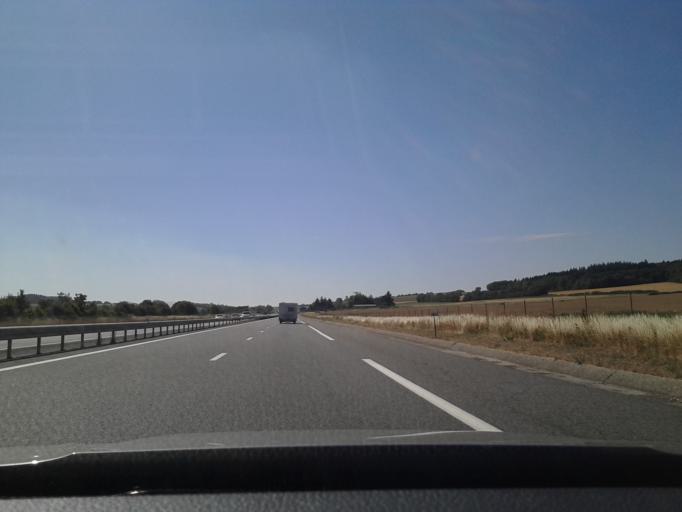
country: FR
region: Midi-Pyrenees
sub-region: Departement de l'Aveyron
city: La Cavalerie
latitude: 43.9899
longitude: 3.1774
